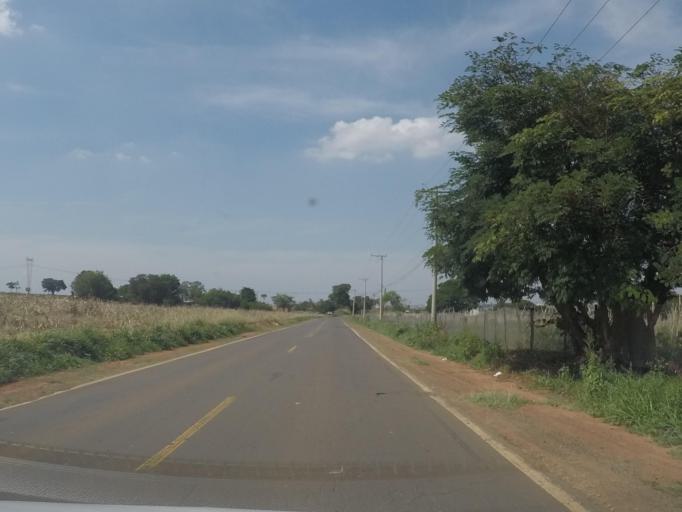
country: BR
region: Sao Paulo
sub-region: Sumare
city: Sumare
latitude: -22.8690
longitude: -47.2972
